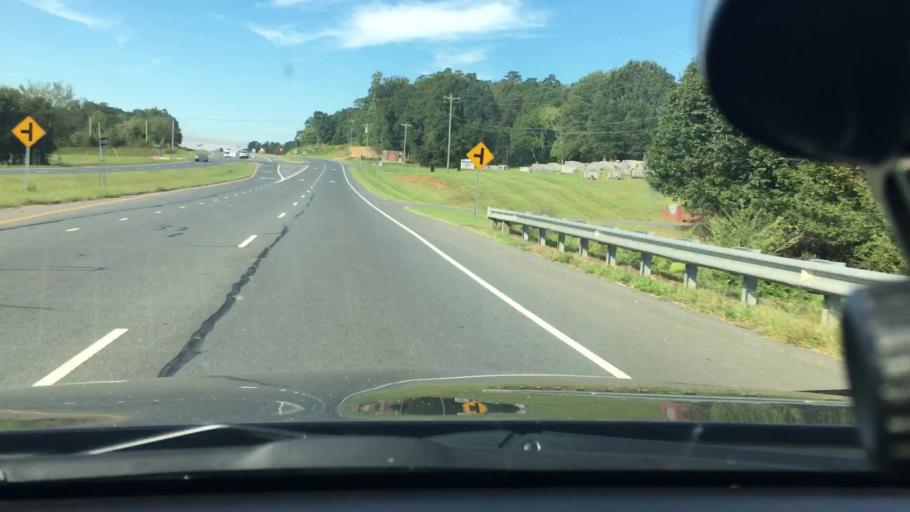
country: US
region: North Carolina
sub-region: Stanly County
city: Oakboro
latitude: 35.2724
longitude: -80.3247
